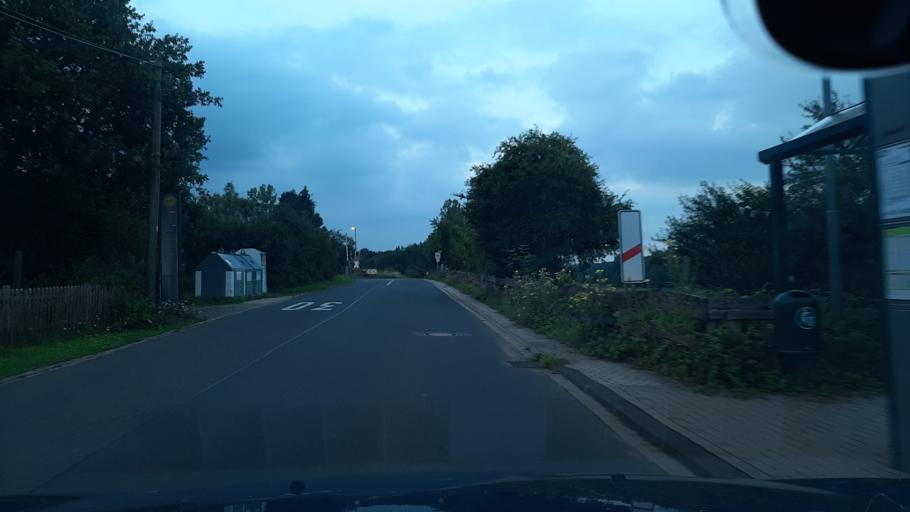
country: DE
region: North Rhine-Westphalia
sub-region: Regierungsbezirk Koln
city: Mechernich
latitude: 50.6030
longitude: 6.6834
